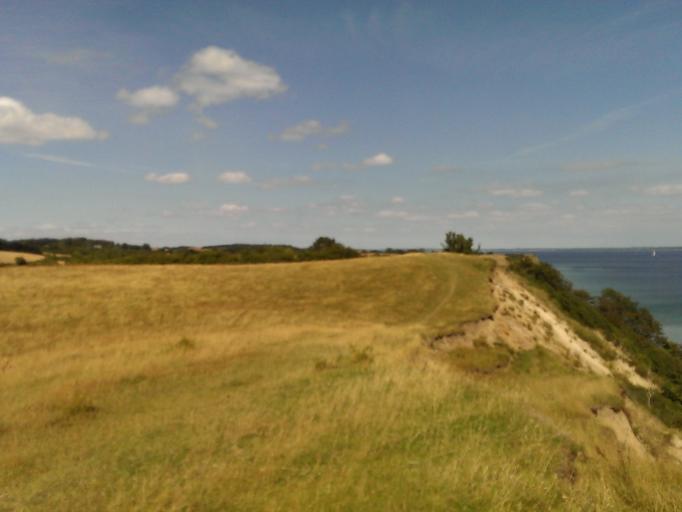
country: DK
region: Central Jutland
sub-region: Syddjurs Kommune
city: Ebeltoft
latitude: 56.1047
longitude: 10.5478
